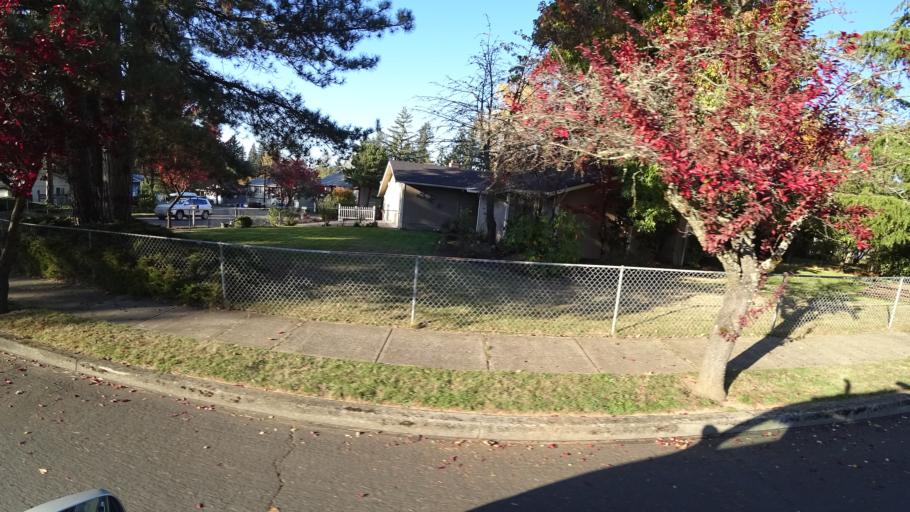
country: US
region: Oregon
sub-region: Multnomah County
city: Gresham
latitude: 45.4857
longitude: -122.4509
